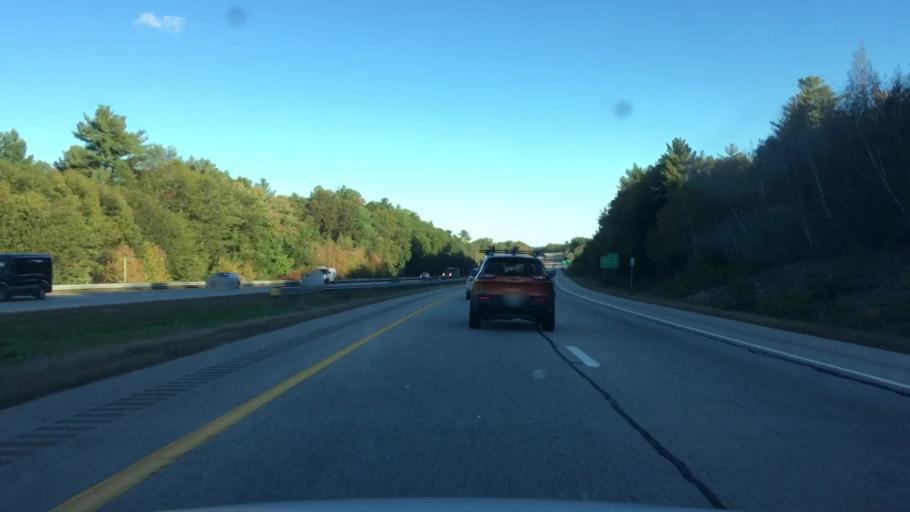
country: US
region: New Hampshire
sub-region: Rockingham County
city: Fremont
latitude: 43.0310
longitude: -71.1315
